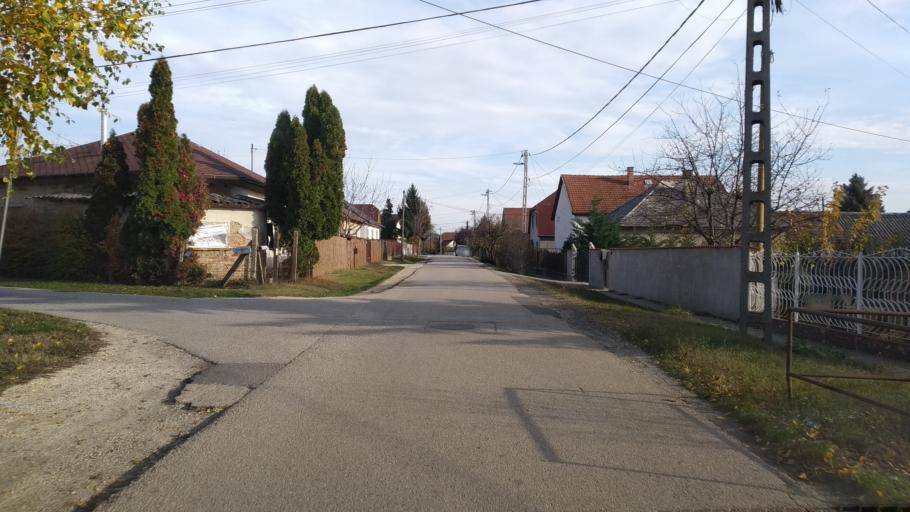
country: HU
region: Pest
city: Gyomro
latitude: 47.4307
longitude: 19.3881
